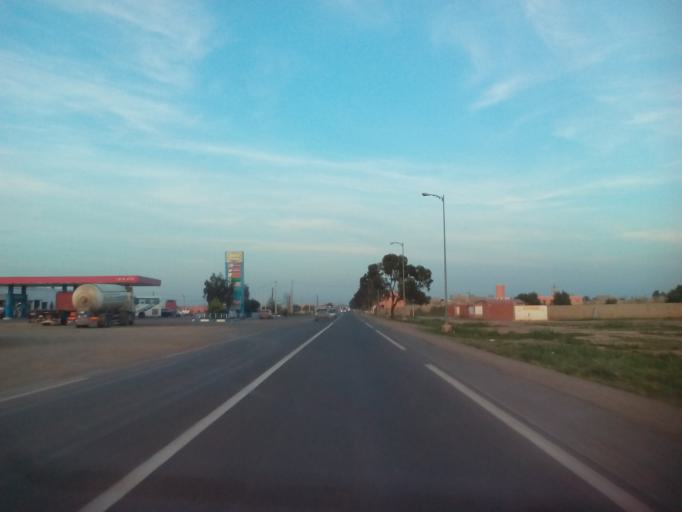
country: MA
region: Marrakech-Tensift-Al Haouz
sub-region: Marrakech
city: Marrakesh
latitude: 31.6284
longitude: -8.2677
